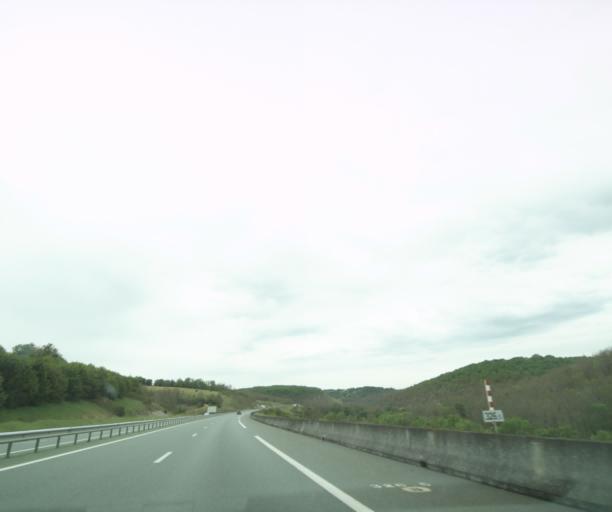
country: FR
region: Midi-Pyrenees
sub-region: Departement du Lot
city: Le Vigan
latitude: 44.7248
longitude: 1.5597
